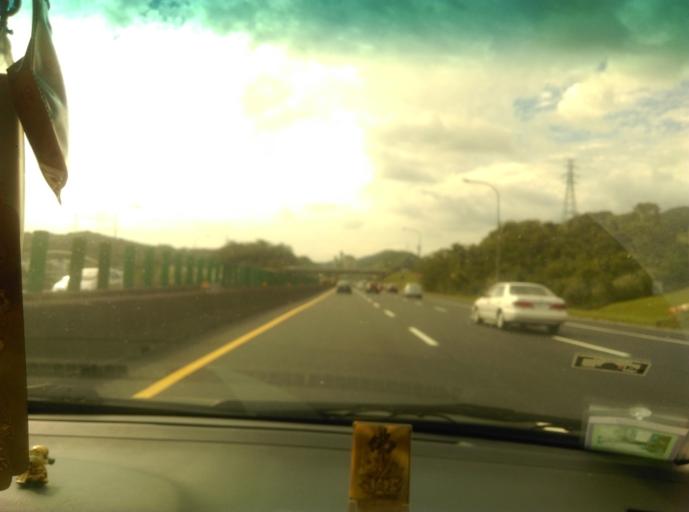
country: TW
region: Taiwan
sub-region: Keelung
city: Keelung
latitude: 25.0875
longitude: 121.6901
